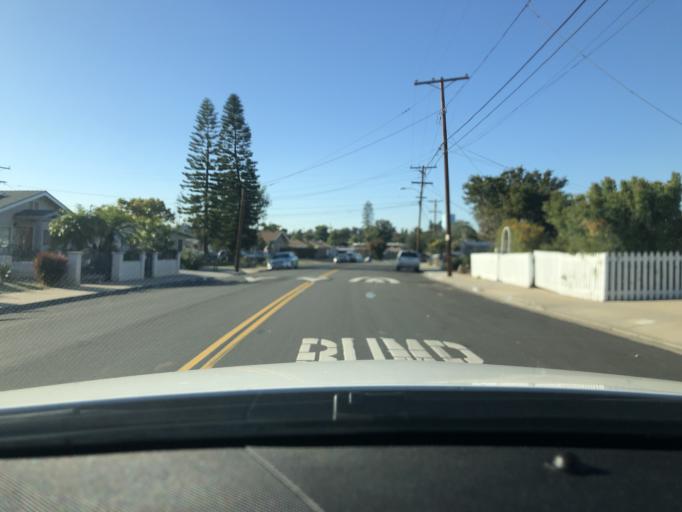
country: US
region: California
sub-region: San Diego County
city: Lemon Grove
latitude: 32.7451
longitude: -117.0604
